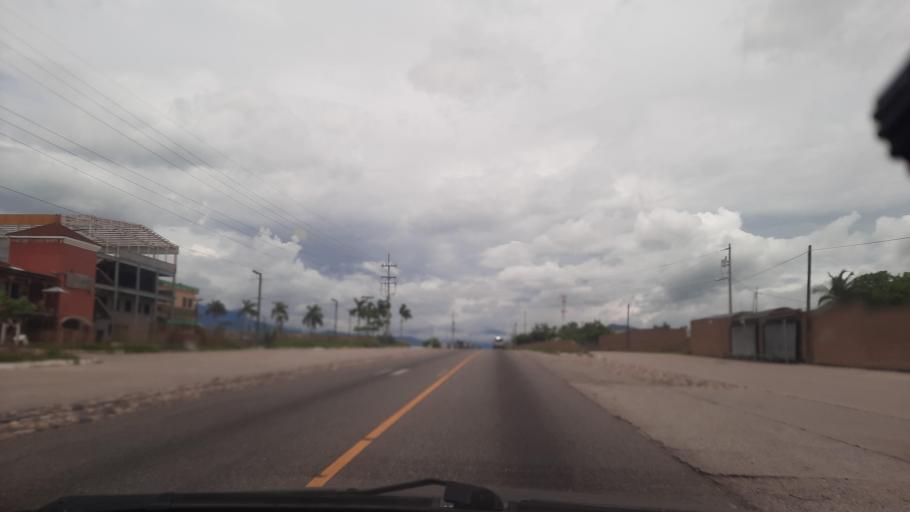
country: GT
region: Zacapa
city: Estanzuela
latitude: 15.0060
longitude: -89.5724
